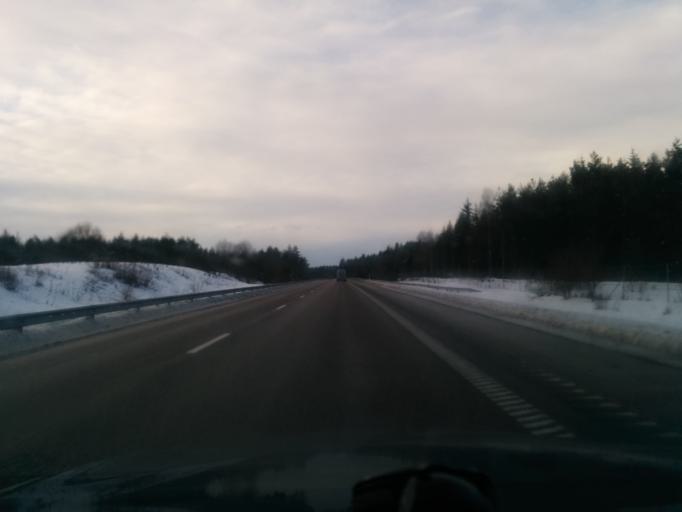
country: SE
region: Uppsala
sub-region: Enkopings Kommun
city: Grillby
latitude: 59.6425
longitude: 17.2101
